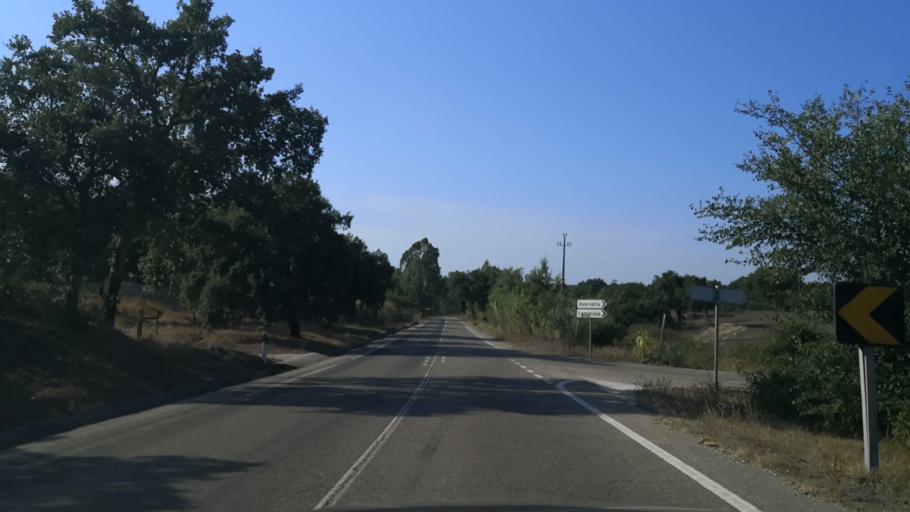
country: PT
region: Santarem
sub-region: Almeirim
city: Fazendas de Almeirim
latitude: 39.0820
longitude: -8.5679
